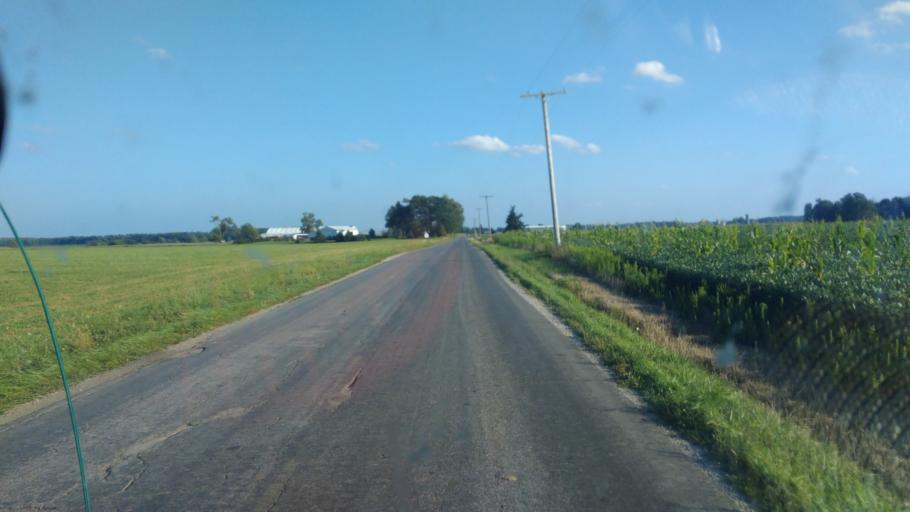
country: US
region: Ohio
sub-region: Huron County
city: Greenwich
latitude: 40.9524
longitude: -82.4586
